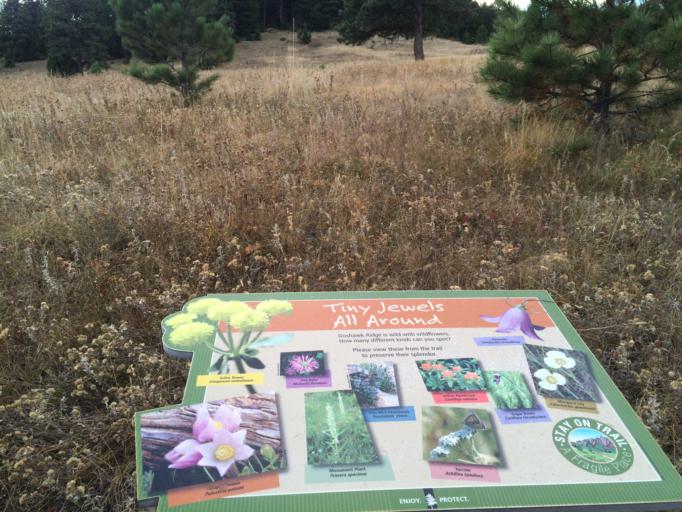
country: US
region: Colorado
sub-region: Boulder County
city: Boulder
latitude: 39.9228
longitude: -105.2780
